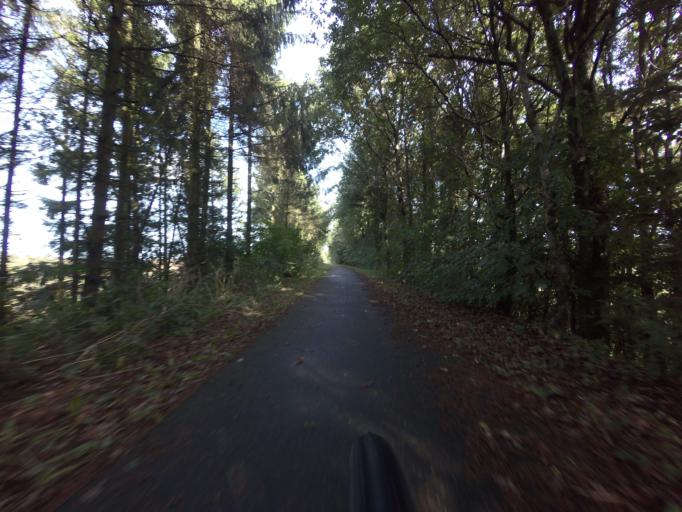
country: DK
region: Central Jutland
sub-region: Viborg Kommune
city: Bjerringbro
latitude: 56.4533
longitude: 9.5840
